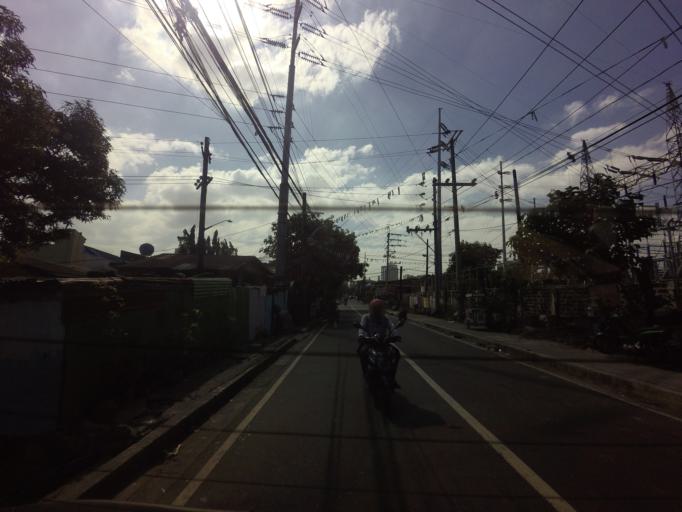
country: PH
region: Metro Manila
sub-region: San Juan
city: San Juan
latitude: 14.6132
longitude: 121.0136
